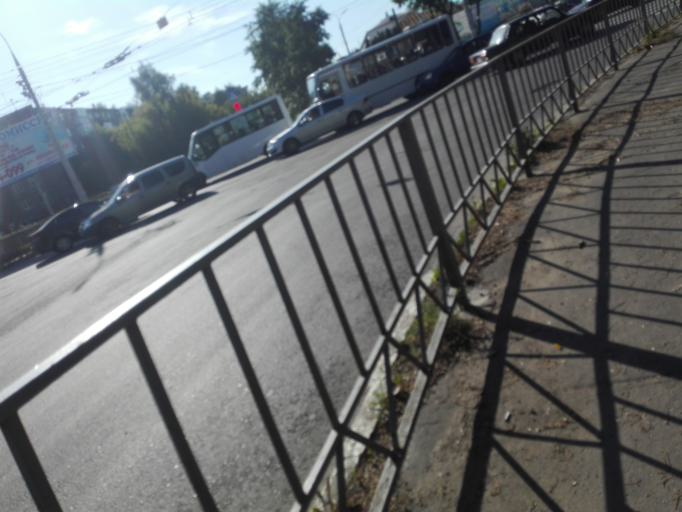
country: RU
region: Orjol
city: Orel
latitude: 52.9812
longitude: 36.0702
